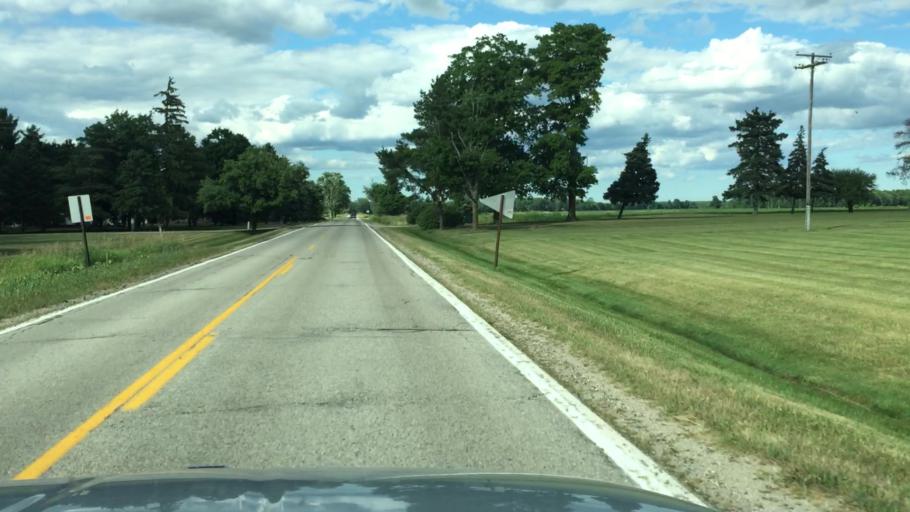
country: US
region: Michigan
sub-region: Saint Clair County
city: Capac
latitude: 43.0675
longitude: -82.9277
